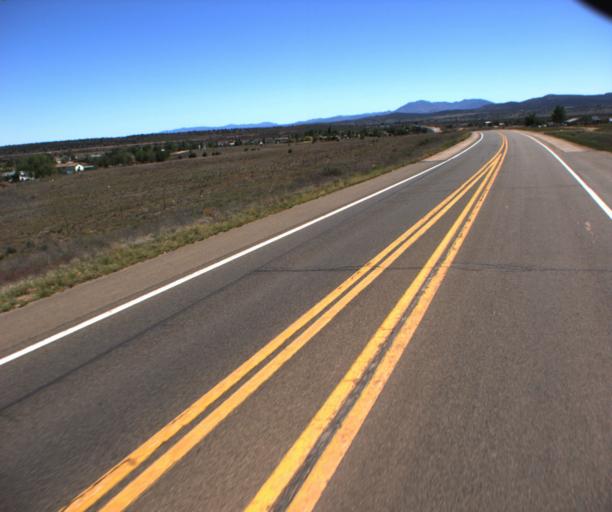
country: US
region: Arizona
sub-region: Yavapai County
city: Paulden
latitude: 34.9086
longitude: -112.4615
